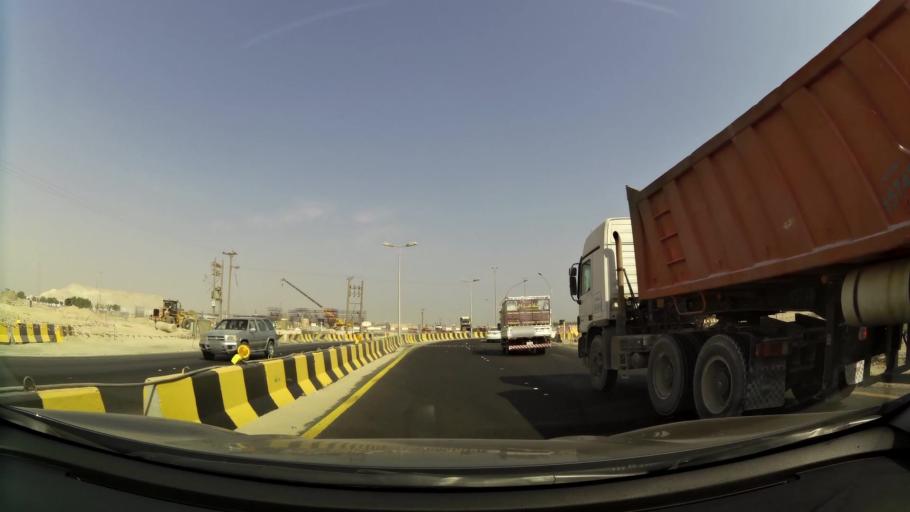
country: KW
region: Al Ahmadi
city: Al Fahahil
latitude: 28.9711
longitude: 48.1283
